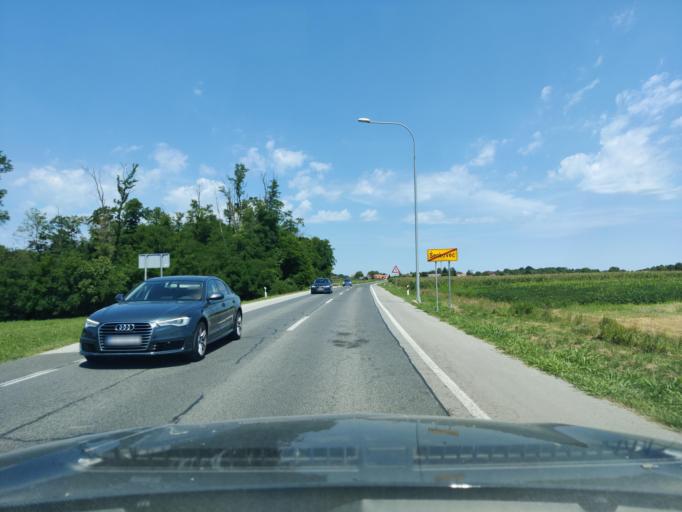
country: HR
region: Medimurska
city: Senkovec
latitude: 46.4178
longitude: 16.4251
